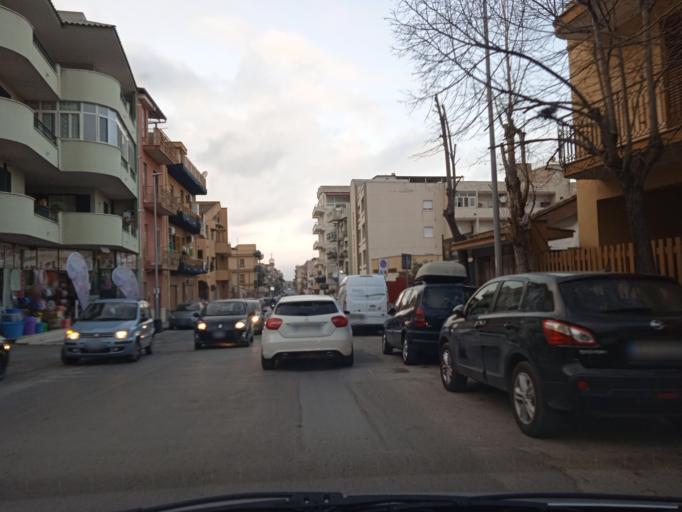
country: IT
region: Sicily
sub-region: Palermo
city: Villabate
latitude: 38.0777
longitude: 13.4385
